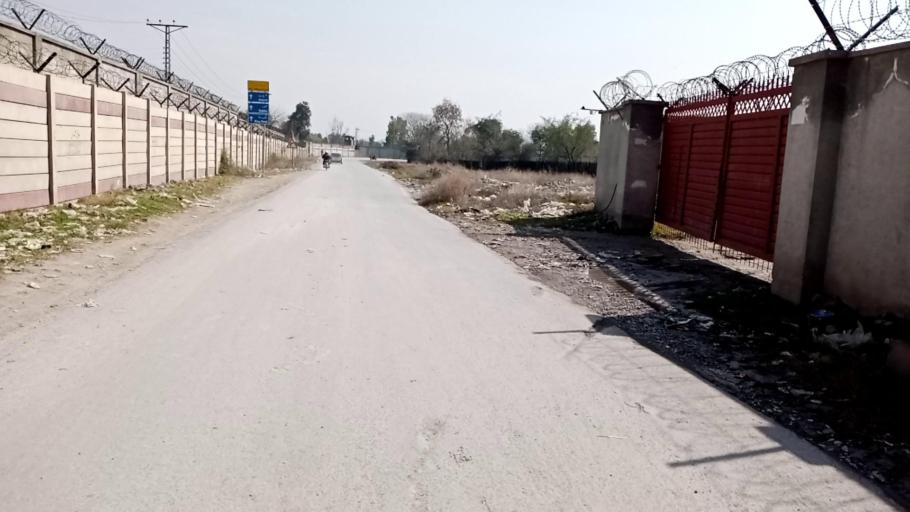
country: PK
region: Khyber Pakhtunkhwa
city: Peshawar
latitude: 33.9944
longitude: 71.5087
